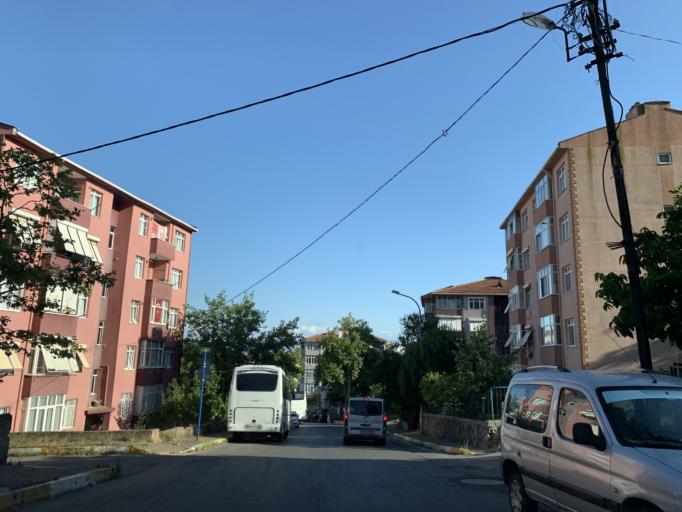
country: TR
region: Istanbul
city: Pendik
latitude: 40.8994
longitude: 29.2489
